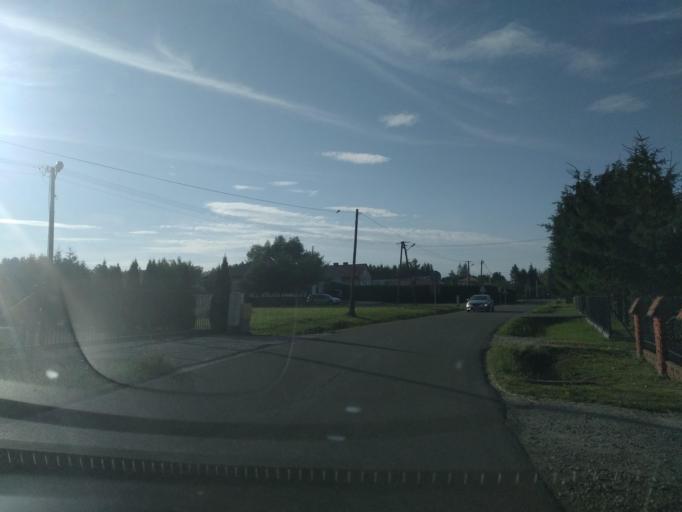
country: PL
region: Subcarpathian Voivodeship
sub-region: Powiat brzozowski
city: Humniska
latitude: 49.6701
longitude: 22.0315
